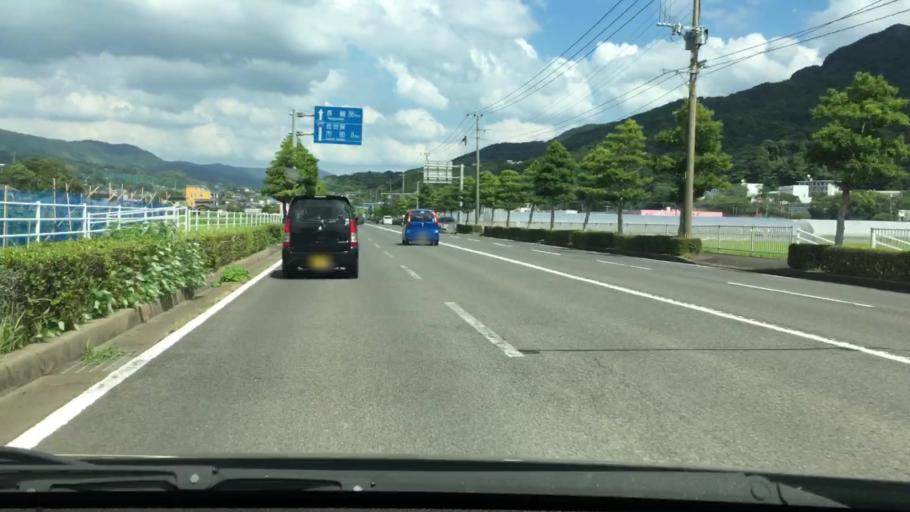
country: JP
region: Nagasaki
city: Sasebo
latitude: 33.2058
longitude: 129.6832
